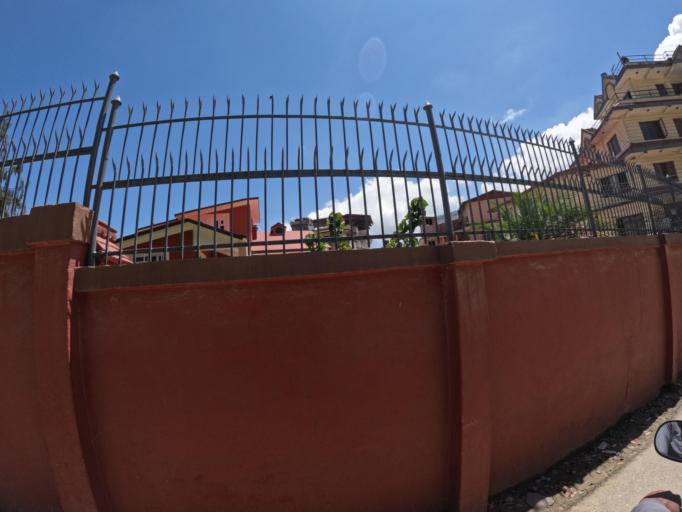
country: NP
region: Central Region
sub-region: Bagmati Zone
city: Kathmandu
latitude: 27.7410
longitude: 85.3270
